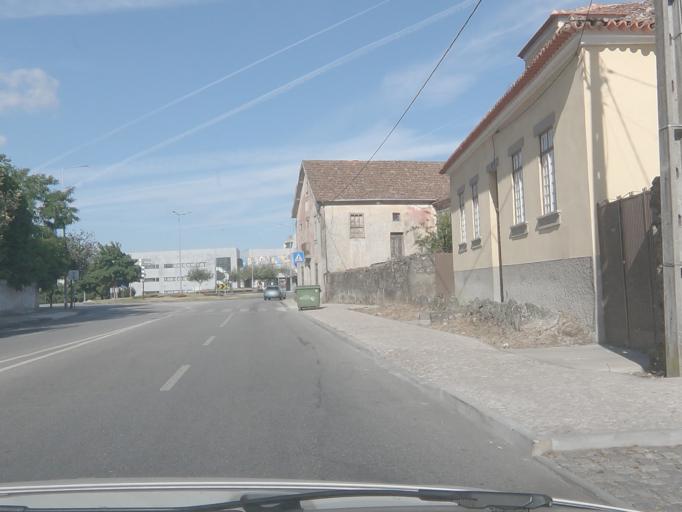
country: PT
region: Viseu
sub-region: Viseu
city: Viseu
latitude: 40.6530
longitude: -7.9092
